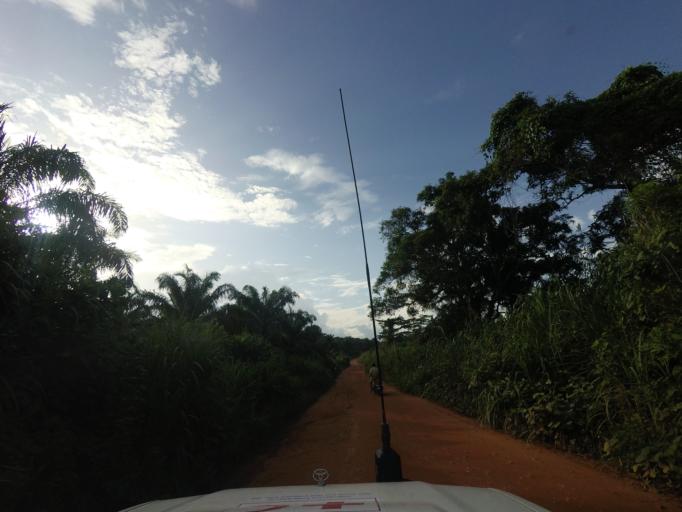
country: GN
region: Nzerekore
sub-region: Nzerekore Prefecture
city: Nzerekore
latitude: 7.6747
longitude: -8.8117
